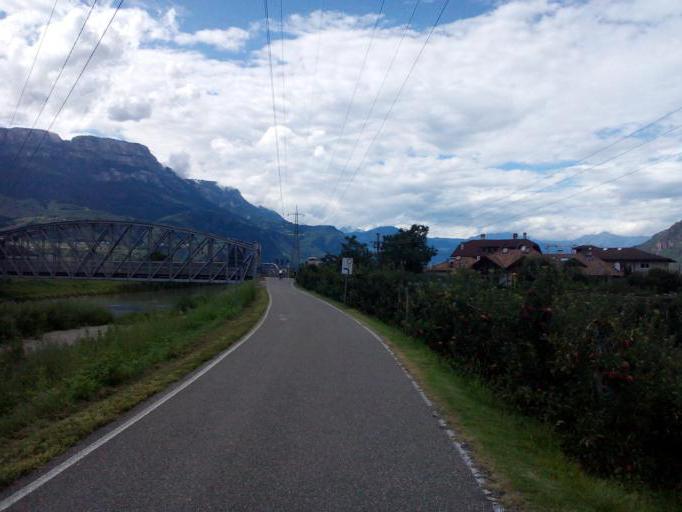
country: IT
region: Trentino-Alto Adige
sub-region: Bolzano
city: Cornaiano
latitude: 46.4828
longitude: 11.3058
